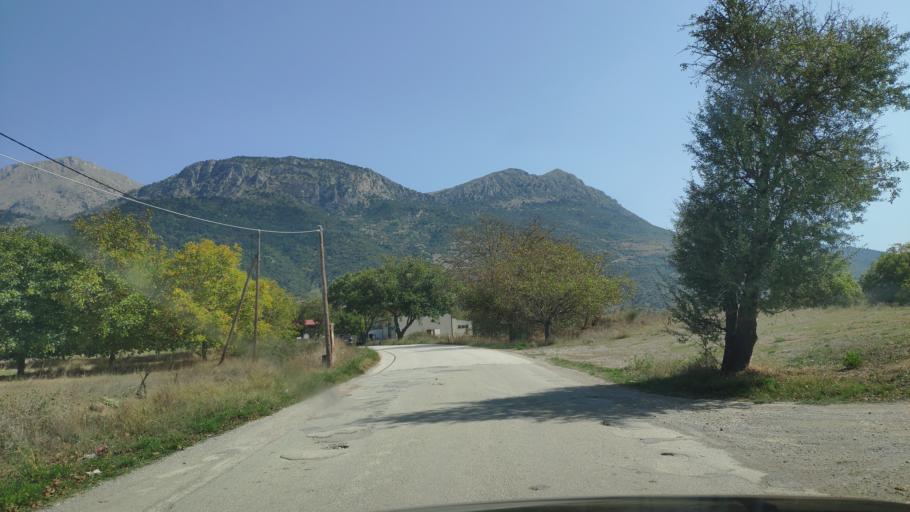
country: GR
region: West Greece
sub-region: Nomos Achaias
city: Kalavryta
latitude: 37.9082
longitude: 22.3194
